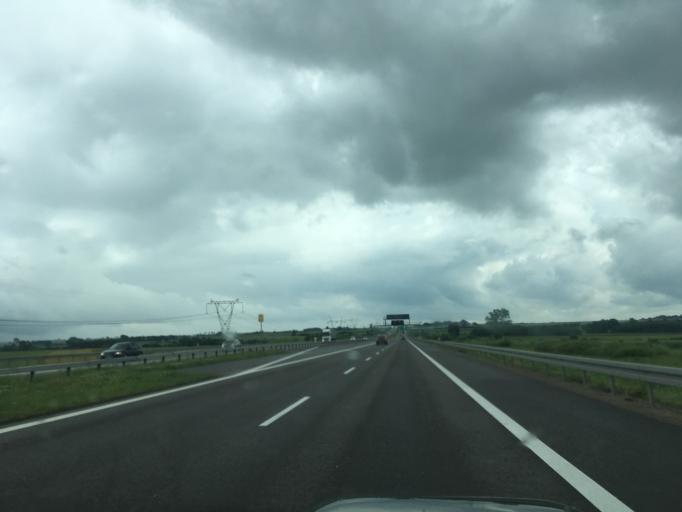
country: PL
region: Lublin Voivodeship
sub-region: Powiat pulawski
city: Markuszow
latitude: 51.3854
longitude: 22.2663
